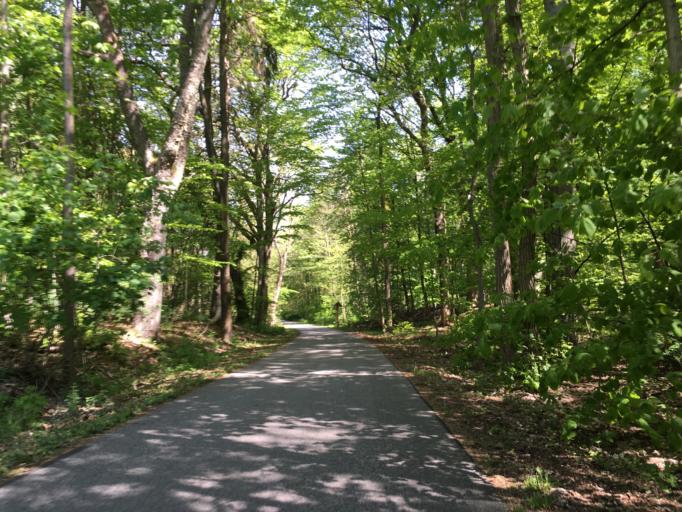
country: DE
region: Brandenburg
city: Bernau bei Berlin
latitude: 52.6934
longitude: 13.5407
